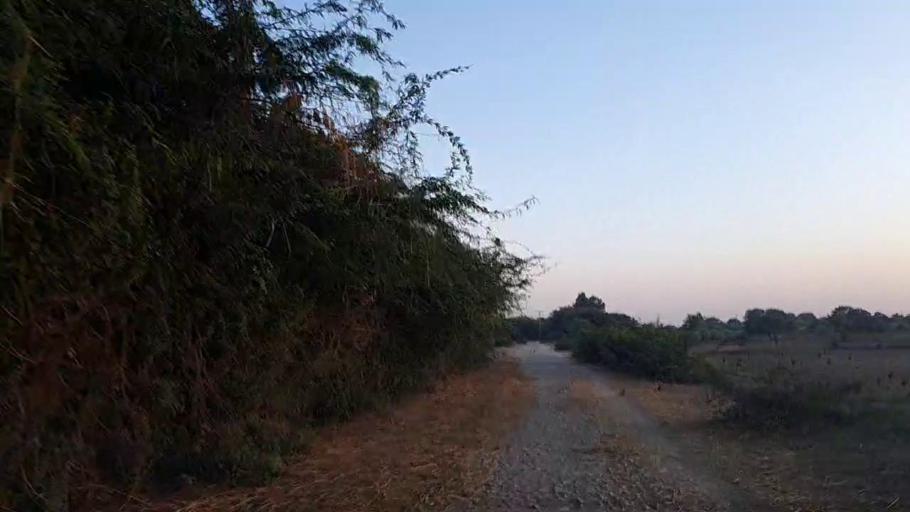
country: PK
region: Sindh
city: Mirpur Batoro
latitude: 24.6374
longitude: 68.1904
